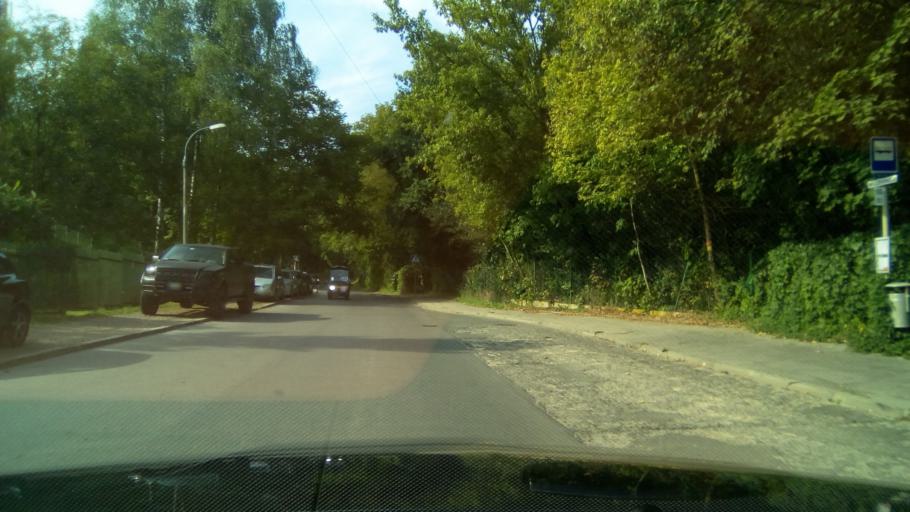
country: PL
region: Lesser Poland Voivodeship
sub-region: Krakow
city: Krakow
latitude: 50.0497
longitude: 19.9033
